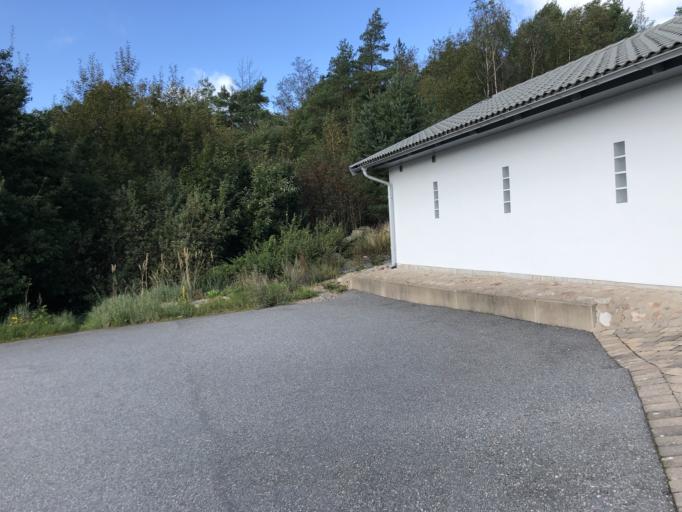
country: SE
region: Vaestra Goetaland
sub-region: Goteborg
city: Torslanda
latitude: 57.7472
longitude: 11.8204
